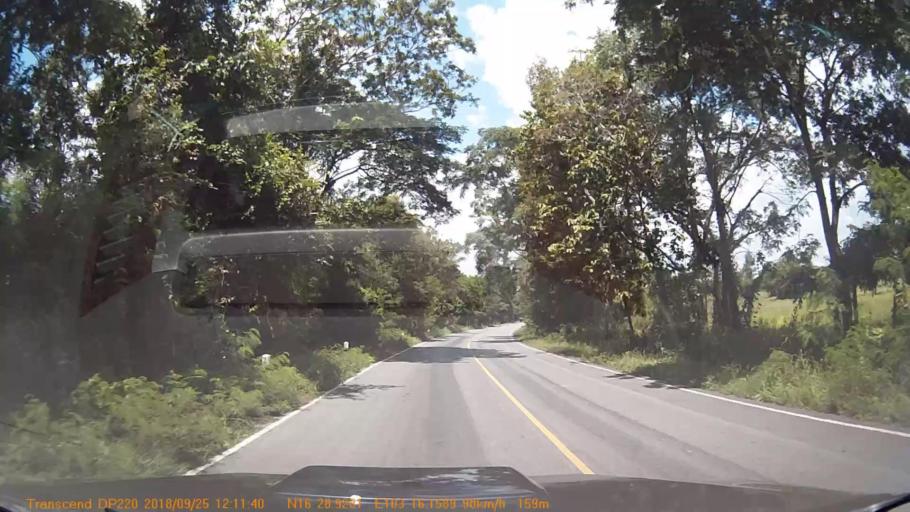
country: TH
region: Kalasin
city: Huai Mek
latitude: 16.4823
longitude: 103.2693
